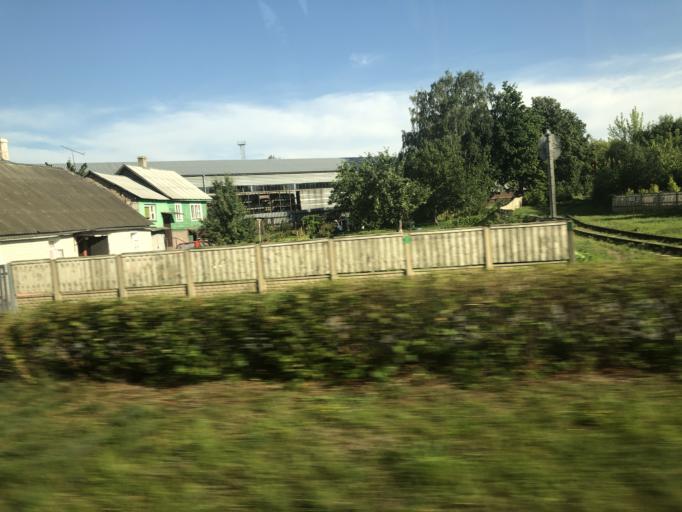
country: BY
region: Grodnenskaya
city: Hrodna
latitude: 53.6574
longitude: 23.8051
